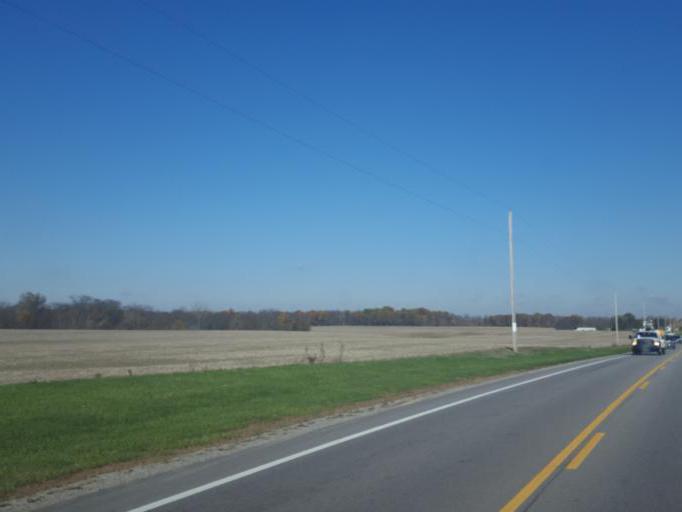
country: US
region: Ohio
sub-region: Wyandot County
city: Carey
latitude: 40.9417
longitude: -83.2718
